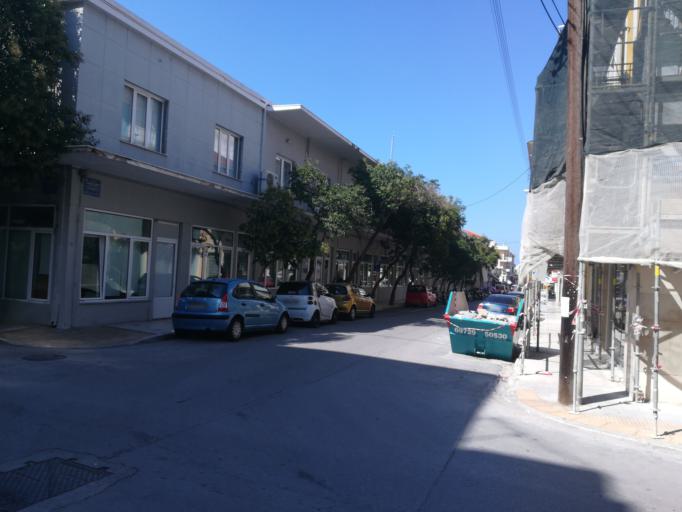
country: GR
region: Crete
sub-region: Nomos Chanias
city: Chania
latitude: 35.5118
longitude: 24.0195
